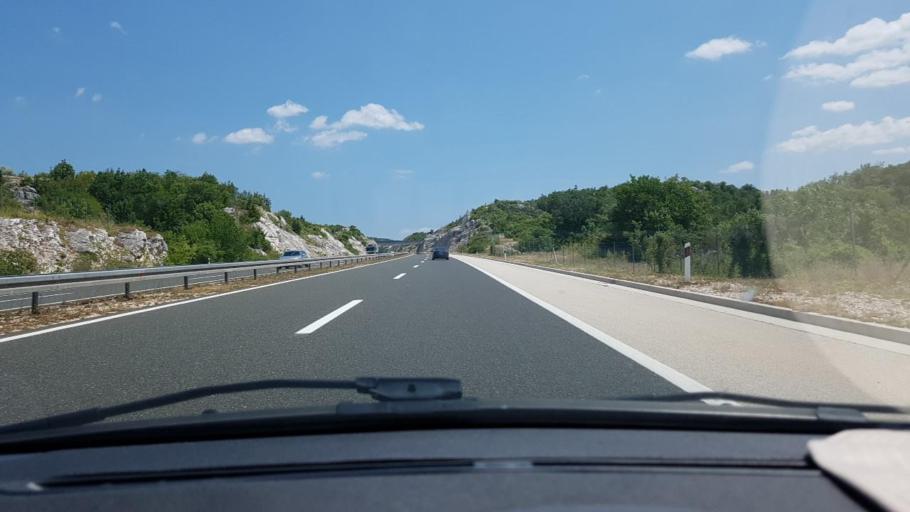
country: HR
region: Splitsko-Dalmatinska
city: Grubine
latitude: 43.3827
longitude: 17.0724
